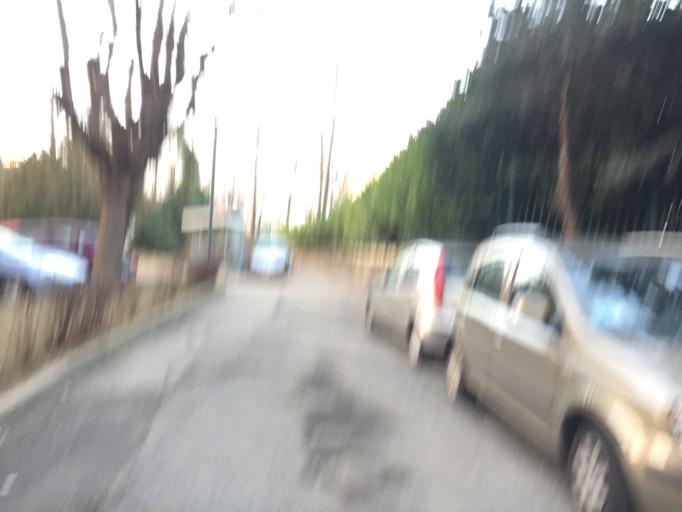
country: IT
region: Piedmont
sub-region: Provincia di Torino
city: Gerbido
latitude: 45.0402
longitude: 7.6190
